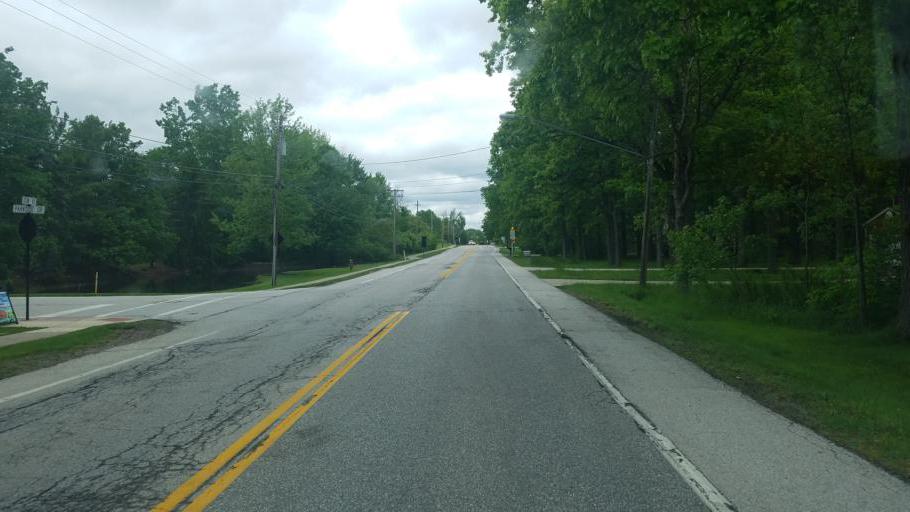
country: US
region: Ohio
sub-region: Summit County
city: Hudson
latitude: 41.2662
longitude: -81.4110
